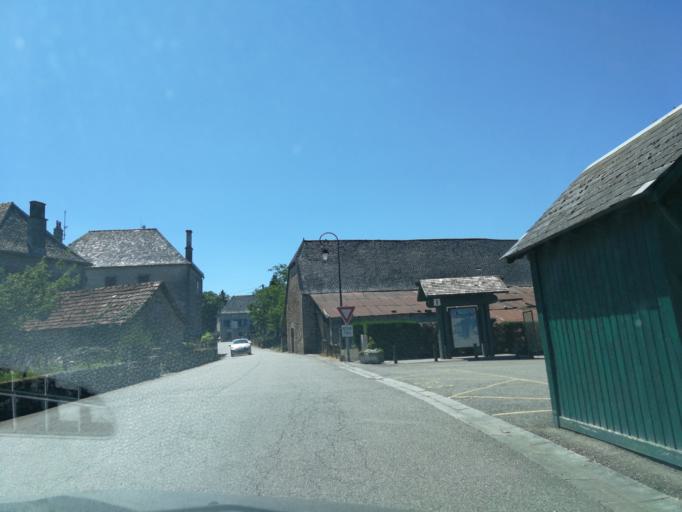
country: FR
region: Limousin
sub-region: Departement de la Correze
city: Argentat
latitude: 45.0394
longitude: 1.9537
